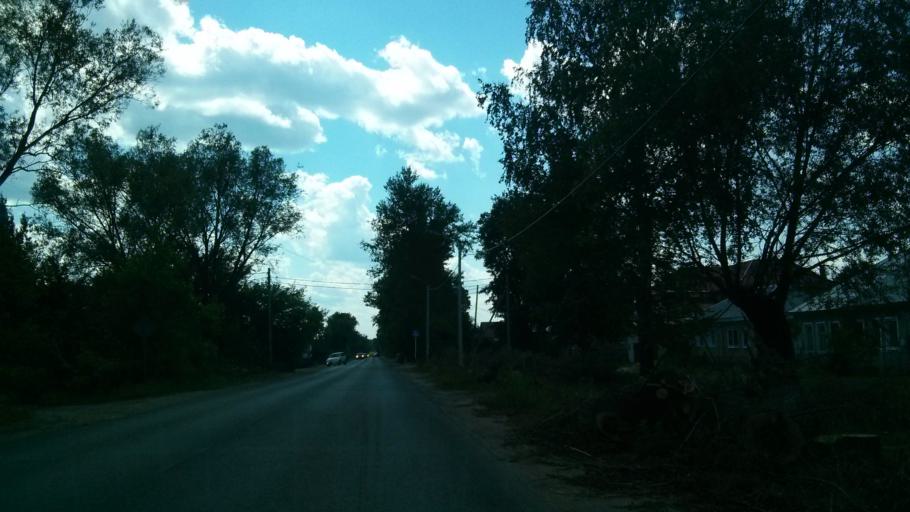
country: RU
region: Vladimir
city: Murom
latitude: 55.5333
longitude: 41.9691
